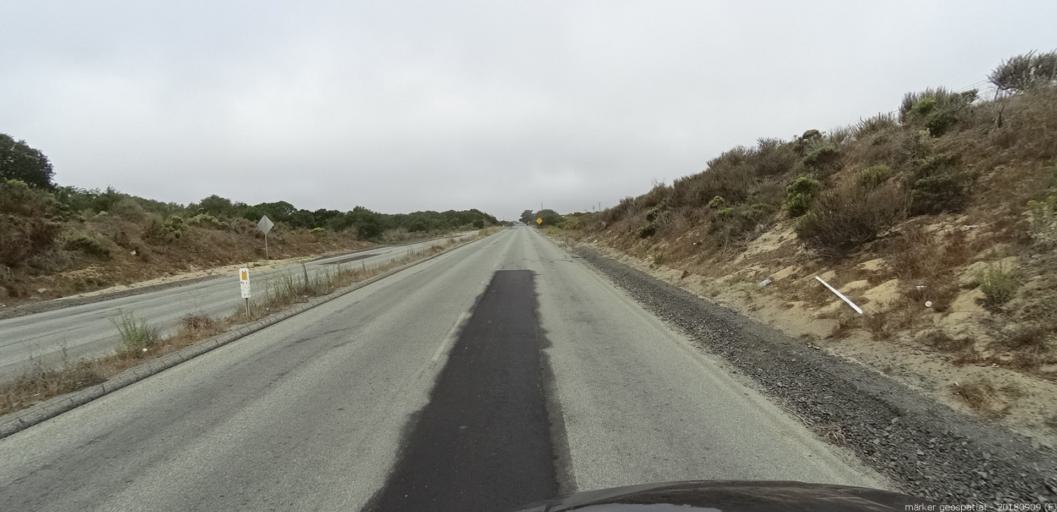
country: US
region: California
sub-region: Monterey County
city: Marina
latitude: 36.6634
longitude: -121.7493
